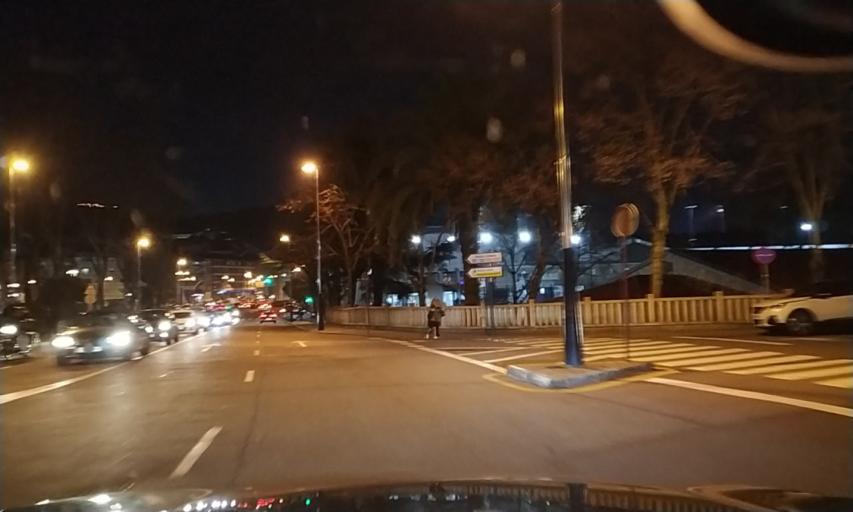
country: ES
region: Galicia
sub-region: Provincia de Ourense
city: Ourense
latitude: 42.3434
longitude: -7.8685
